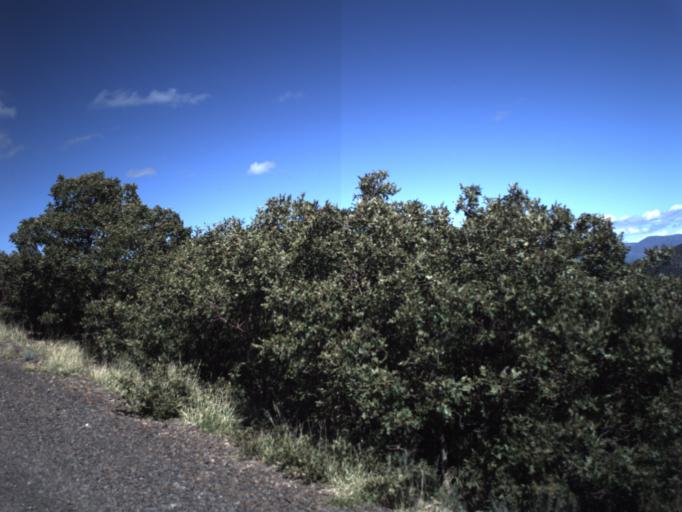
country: US
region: Utah
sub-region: Piute County
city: Junction
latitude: 38.2562
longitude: -112.3184
